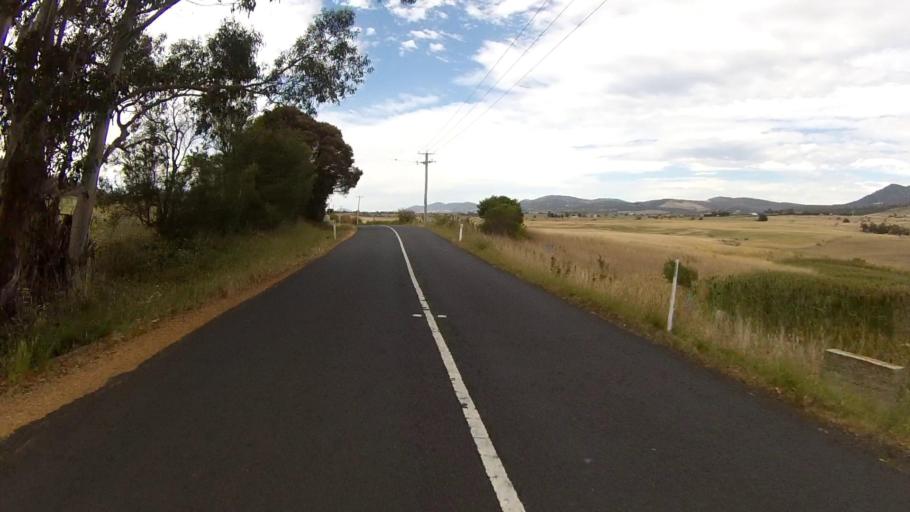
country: AU
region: Tasmania
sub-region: Clarence
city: Cambridge
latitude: -42.7242
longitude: 147.3968
